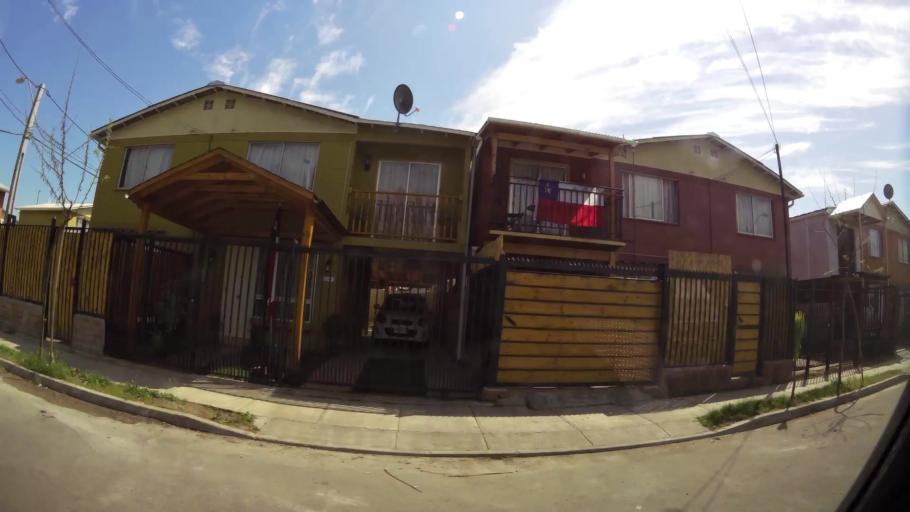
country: CL
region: Santiago Metropolitan
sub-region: Provincia de Talagante
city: Talagante
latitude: -33.6699
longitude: -70.9209
